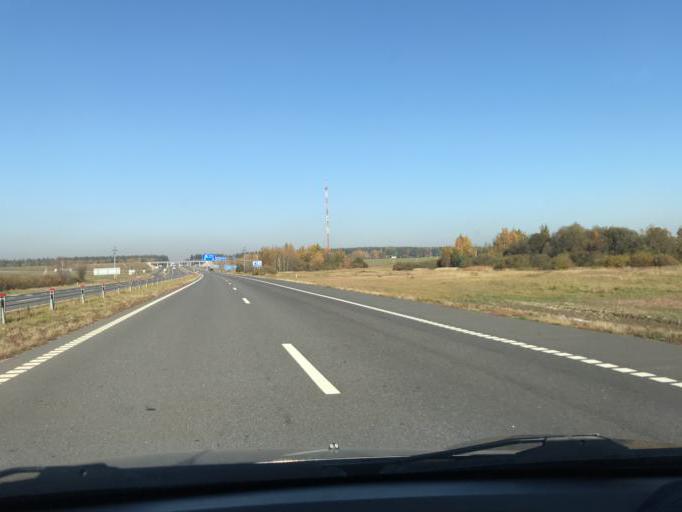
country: BY
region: Mogilev
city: Babruysk
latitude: 53.1775
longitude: 29.3593
